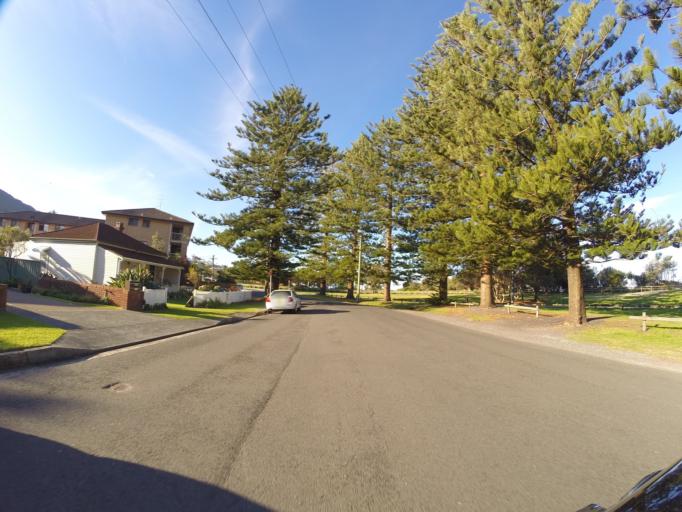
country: AU
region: New South Wales
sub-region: Wollongong
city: Bulli
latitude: -34.3153
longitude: 150.9275
